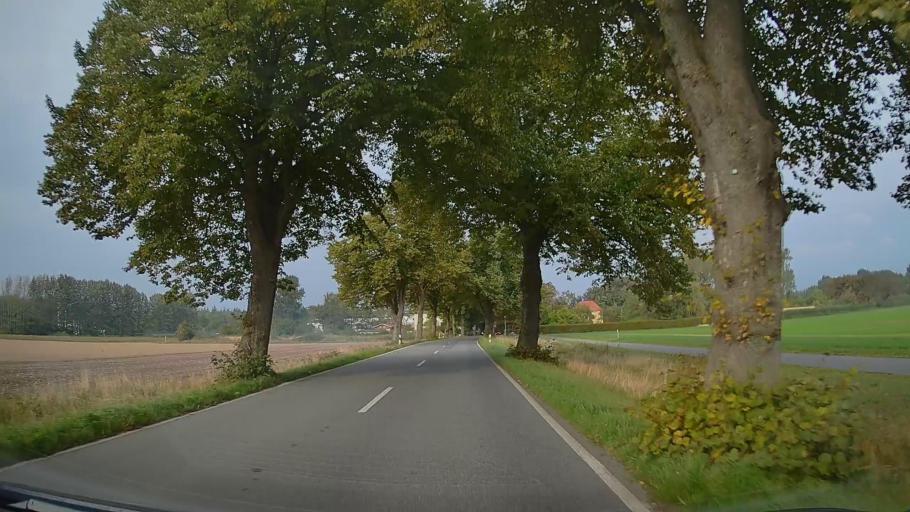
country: DE
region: Mecklenburg-Vorpommern
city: Bad Doberan
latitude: 54.1359
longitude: 11.8362
